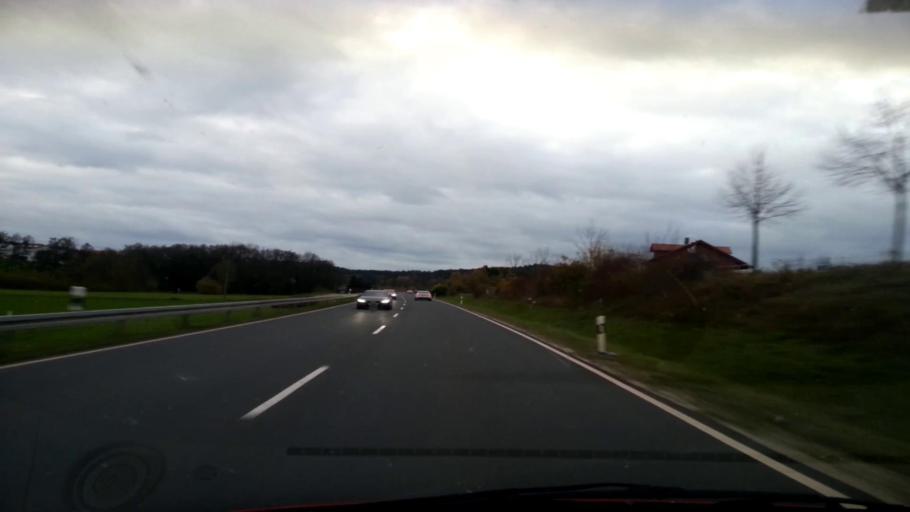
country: DE
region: Bavaria
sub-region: Upper Franconia
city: Schneckenlohe
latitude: 50.2139
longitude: 11.2043
